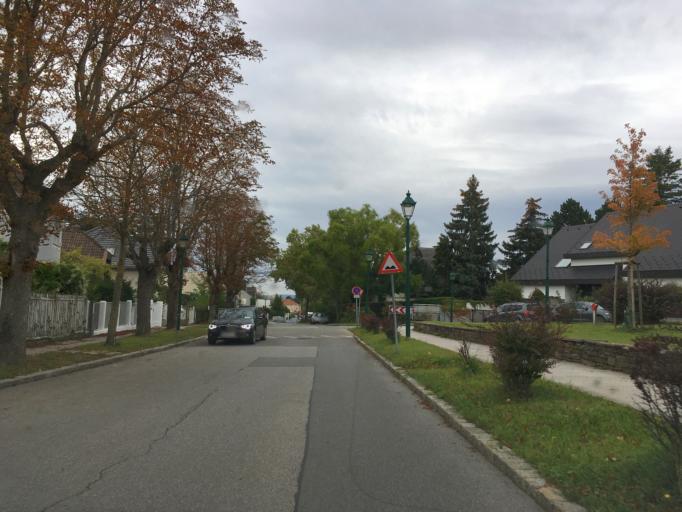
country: AT
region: Lower Austria
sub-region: Politischer Bezirk Modling
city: Maria Enzersdorf
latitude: 48.0950
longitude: 16.2794
